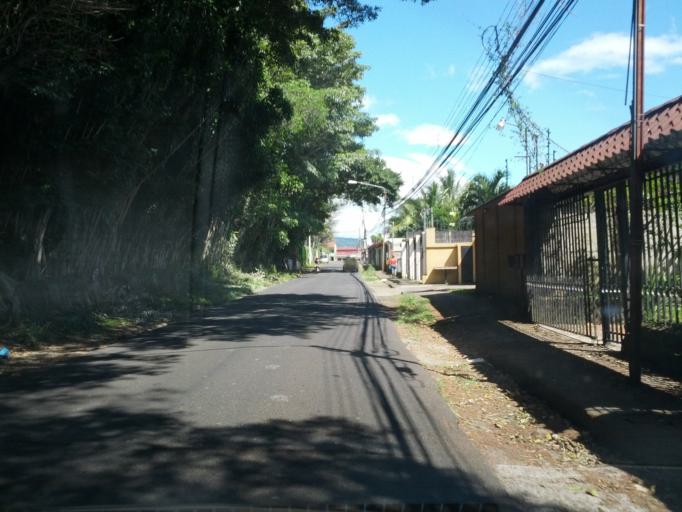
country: CR
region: Alajuela
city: Alajuela
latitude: 10.0217
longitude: -84.2033
